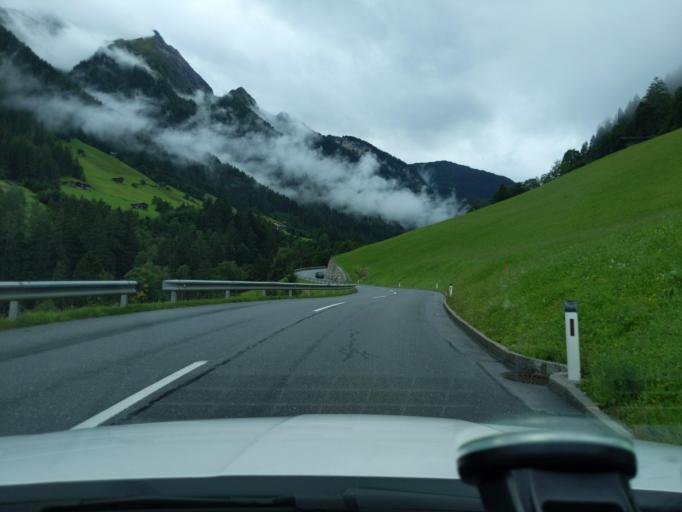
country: AT
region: Tyrol
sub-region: Politischer Bezirk Schwaz
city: Mayrhofen
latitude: 47.1500
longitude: 11.8127
